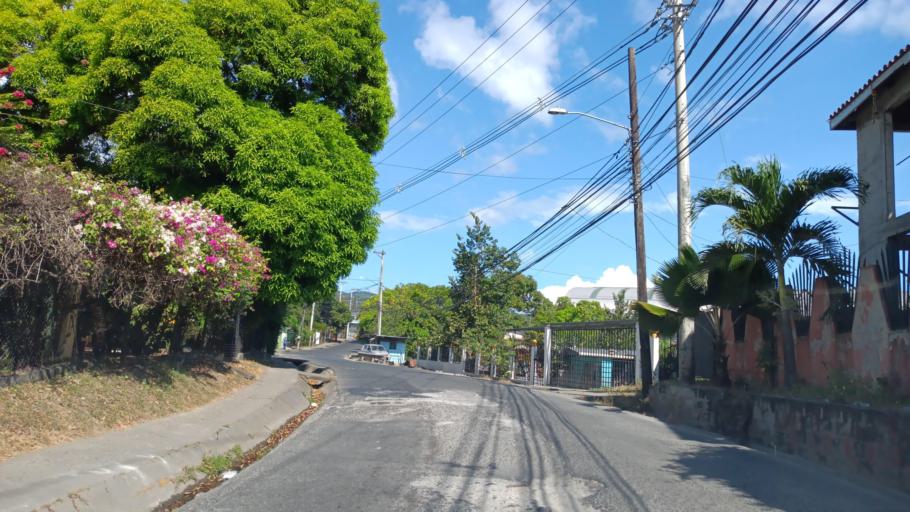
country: PA
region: Panama
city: Tocumen
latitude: 9.1016
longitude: -79.3709
